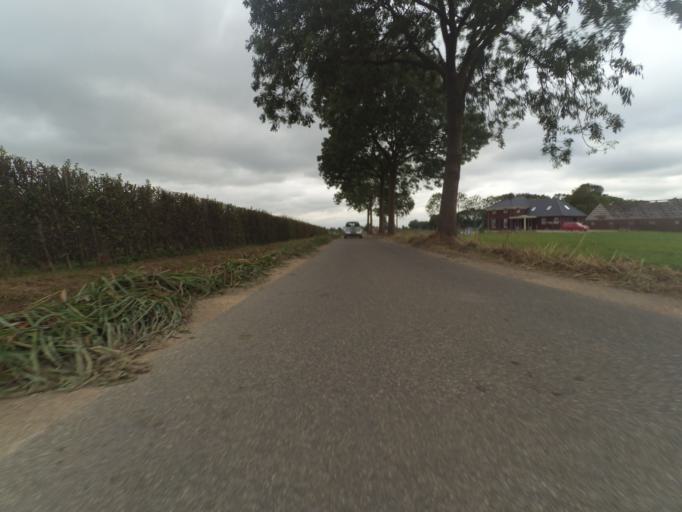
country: NL
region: Gelderland
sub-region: Gemeente Buren
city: Lienden
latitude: 51.9617
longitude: 5.4991
